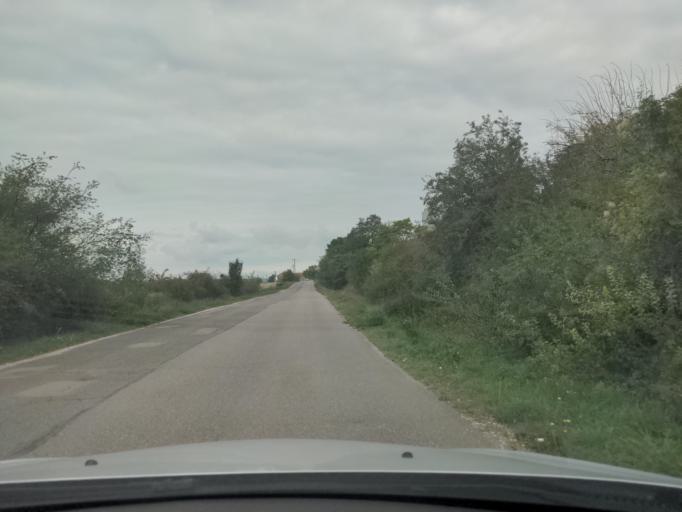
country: FR
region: Bourgogne
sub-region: Departement de la Cote-d'Or
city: Ahuy
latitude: 47.3617
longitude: 5.0381
